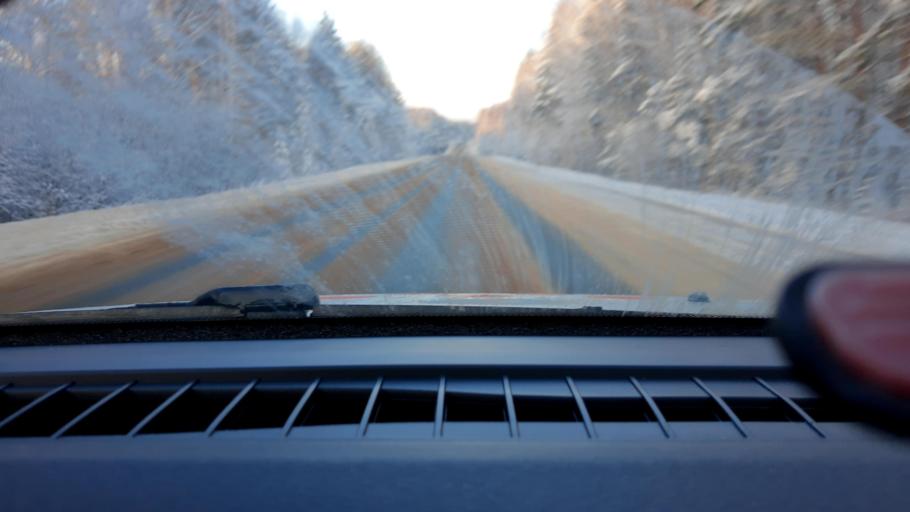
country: RU
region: Nizjnij Novgorod
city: Tonkino
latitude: 57.2923
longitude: 46.4622
